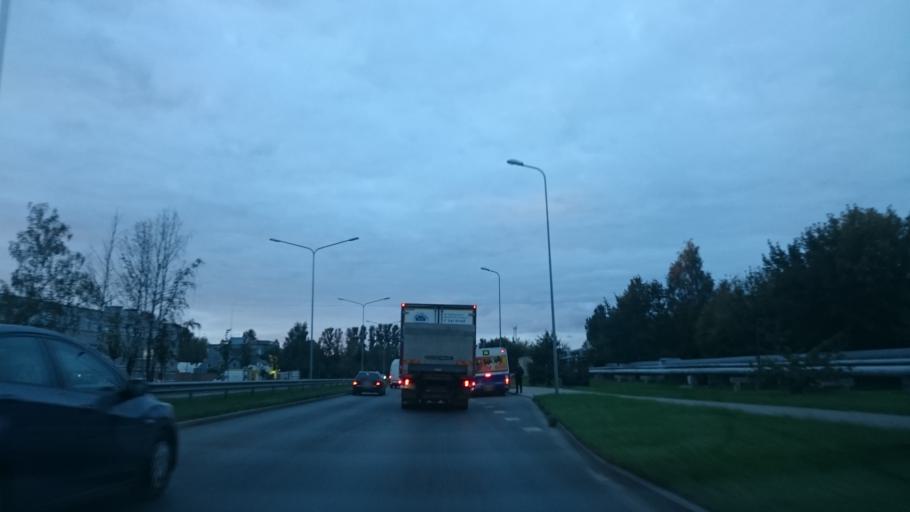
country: LV
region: Kekava
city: Balozi
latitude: 56.9205
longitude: 24.1937
